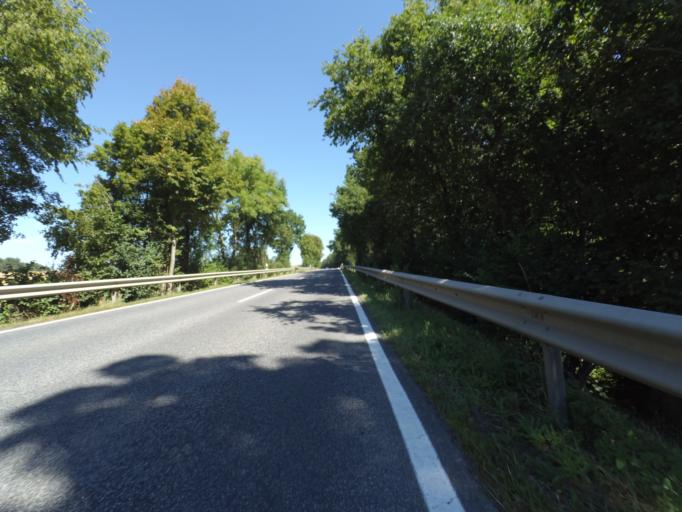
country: DE
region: Rheinland-Pfalz
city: Alflen
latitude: 50.1637
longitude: 7.0386
